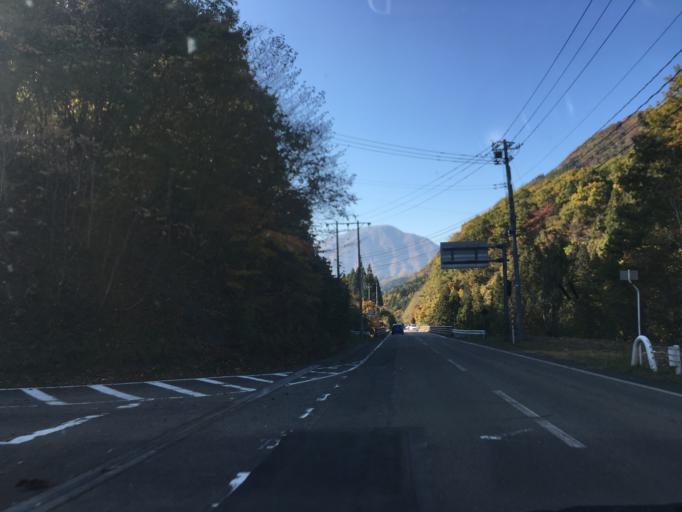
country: JP
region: Fukushima
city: Inawashiro
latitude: 37.2973
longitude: 139.9543
